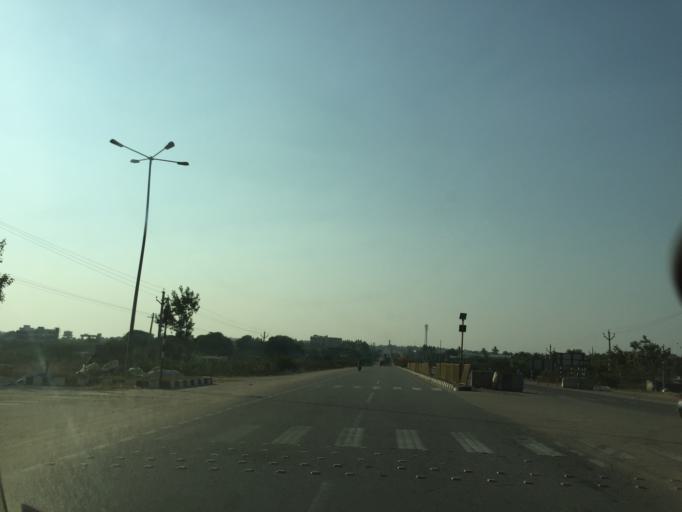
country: IN
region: Telangana
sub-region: Nalgonda
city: Bhongir
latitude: 17.5012
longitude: 78.8822
